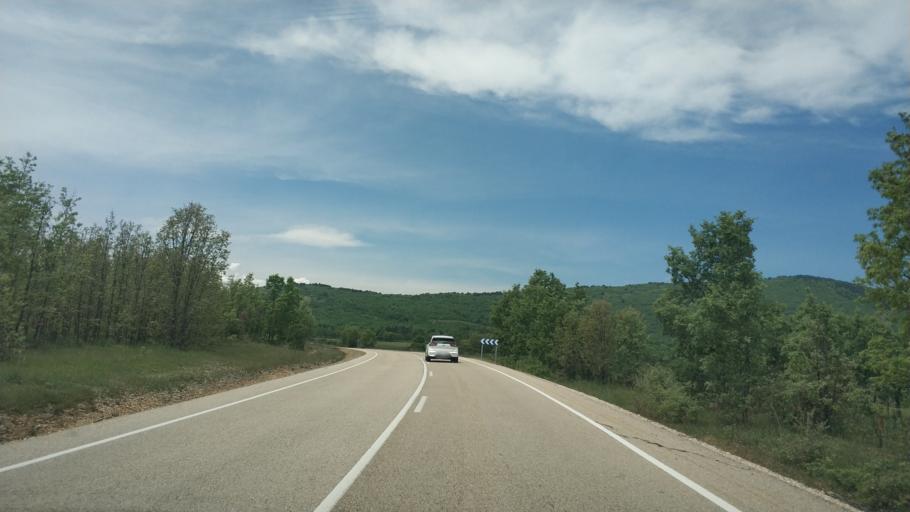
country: ES
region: Castille and Leon
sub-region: Provincia de Soria
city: Vinuesa
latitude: 41.8878
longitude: -2.6907
